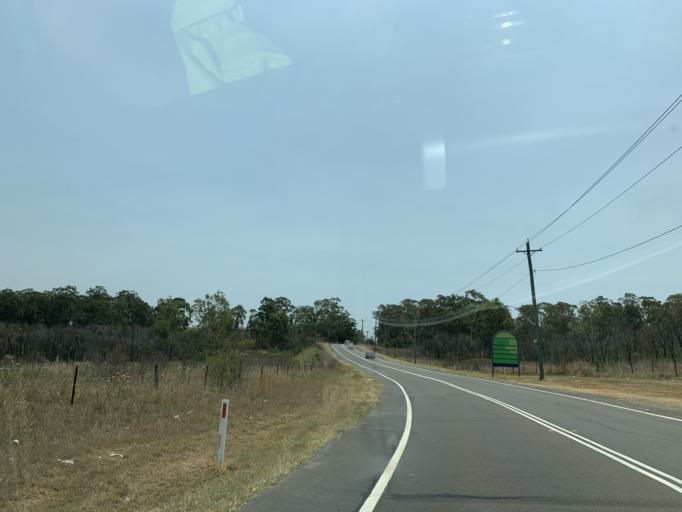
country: AU
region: New South Wales
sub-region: Fairfield
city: Horsley Park
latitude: -33.8316
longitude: 150.8738
